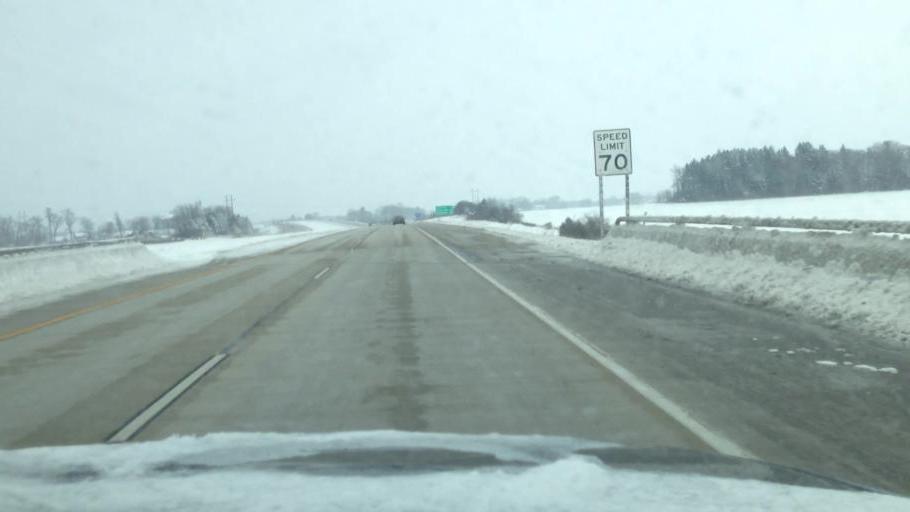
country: US
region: Wisconsin
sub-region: Walworth County
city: Elkhorn
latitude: 42.6989
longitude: -88.4934
